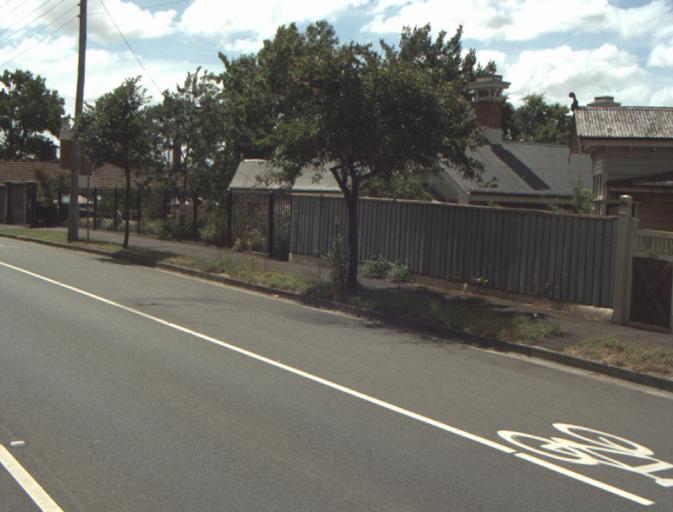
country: AU
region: Tasmania
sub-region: Launceston
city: East Launceston
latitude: -41.4381
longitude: 147.1583
